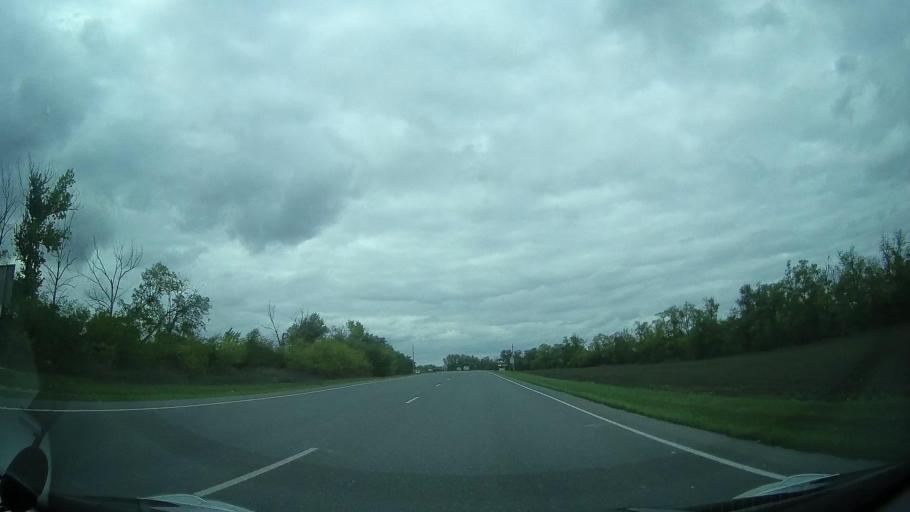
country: RU
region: Rostov
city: Mechetinskaya
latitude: 46.7505
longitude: 40.4619
